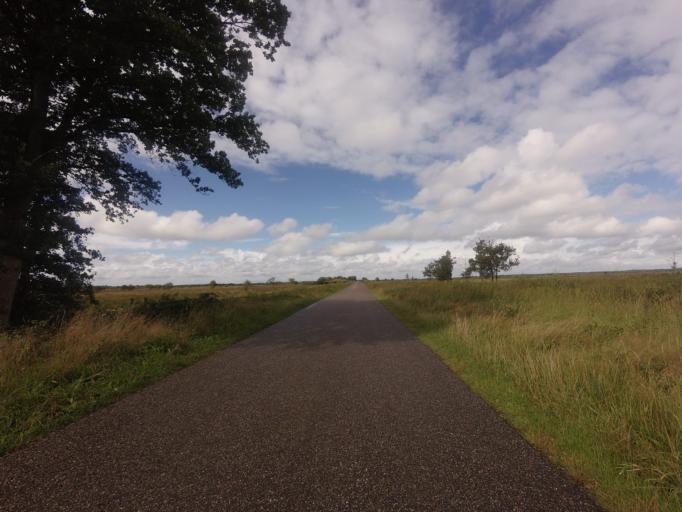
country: NL
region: Drenthe
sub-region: Gemeente Westerveld
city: Dwingeloo
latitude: 52.9965
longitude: 6.3775
